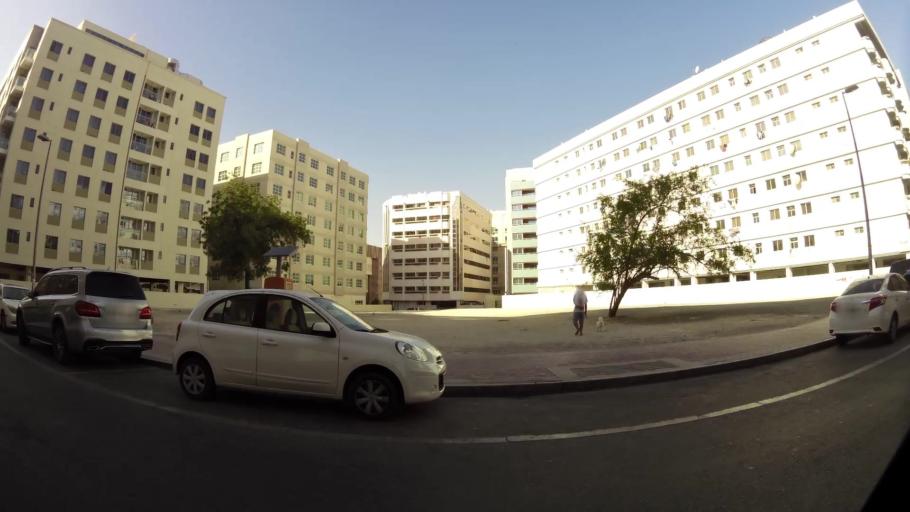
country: AE
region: Ash Shariqah
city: Sharjah
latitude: 25.2565
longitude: 55.2912
